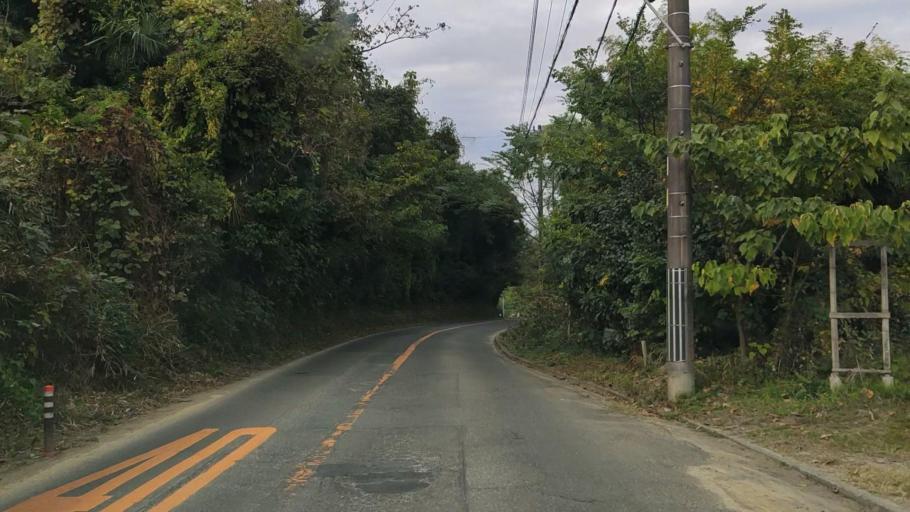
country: JP
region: Shizuoka
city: Shizuoka-shi
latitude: 34.9896
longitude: 138.4551
